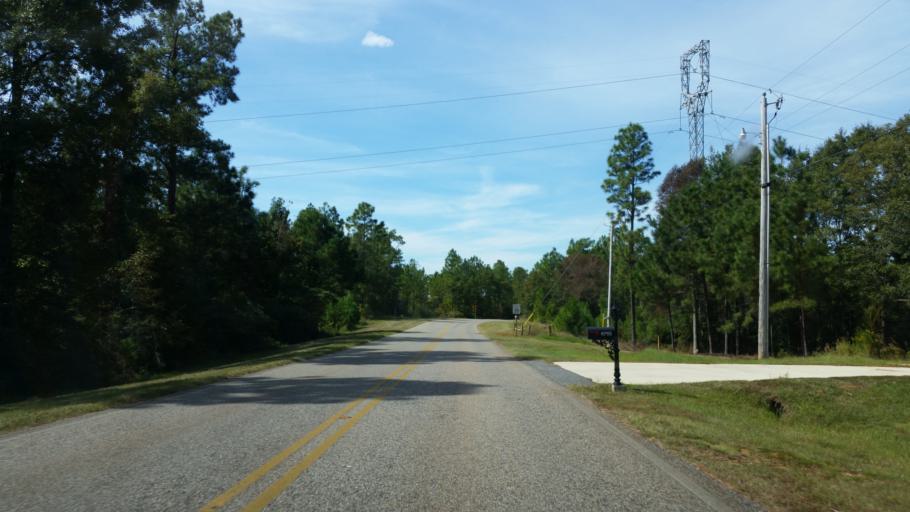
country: US
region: Alabama
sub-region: Baldwin County
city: Spanish Fort
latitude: 30.7356
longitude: -87.8550
